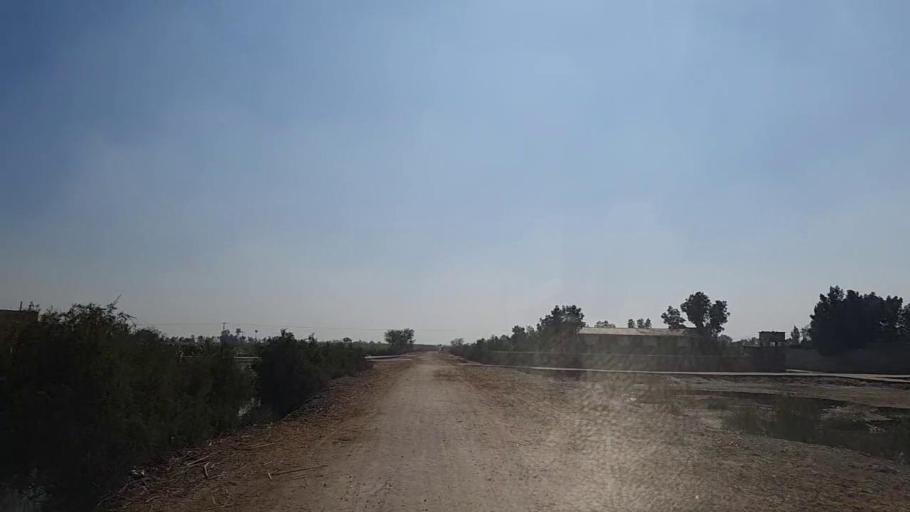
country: PK
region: Sindh
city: Bandhi
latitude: 26.5445
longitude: 68.3320
